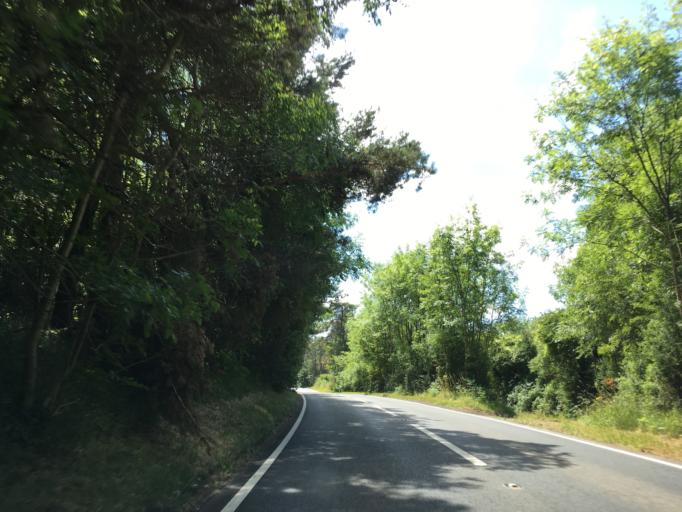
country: GB
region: England
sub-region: Gloucestershire
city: Painswick
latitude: 51.8016
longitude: -2.1968
